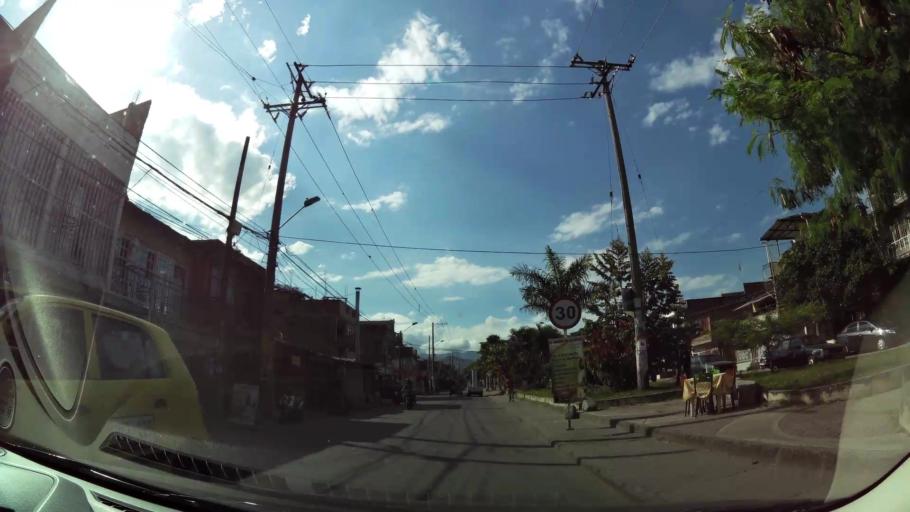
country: CO
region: Valle del Cauca
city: Cali
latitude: 3.4190
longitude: -76.4949
